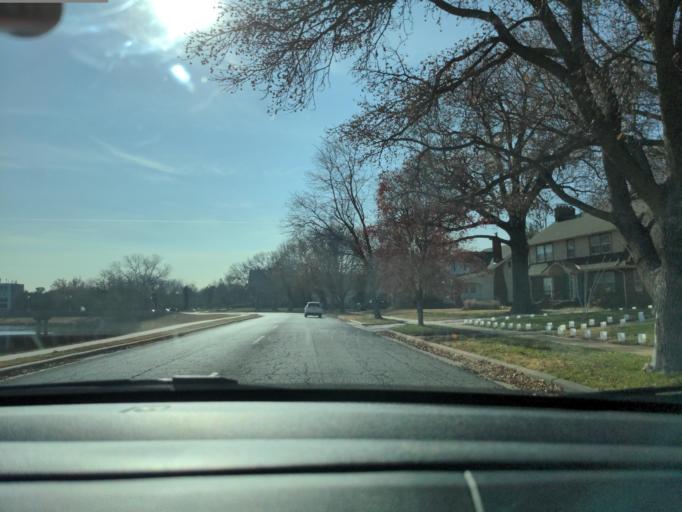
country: US
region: Kansas
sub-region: Sedgwick County
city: Wichita
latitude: 37.7062
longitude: -97.3583
